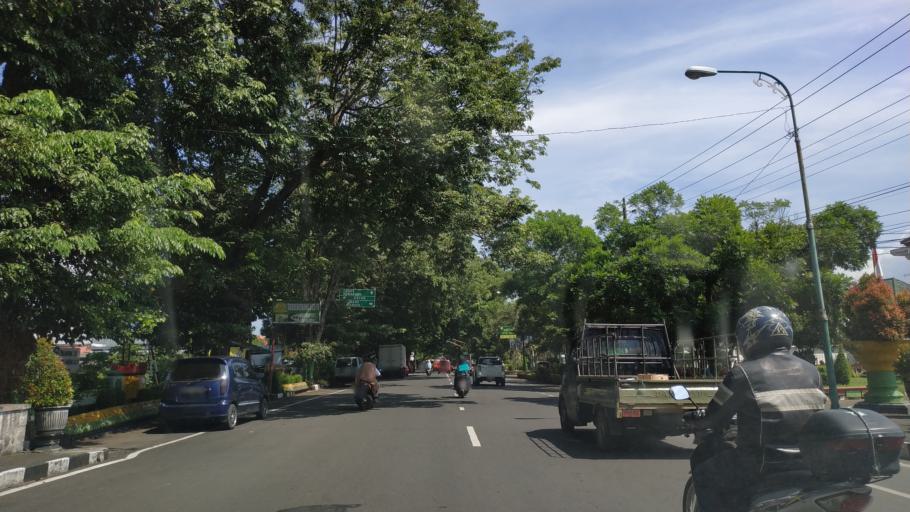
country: ID
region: Central Java
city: Pati
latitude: -6.7518
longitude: 111.0344
